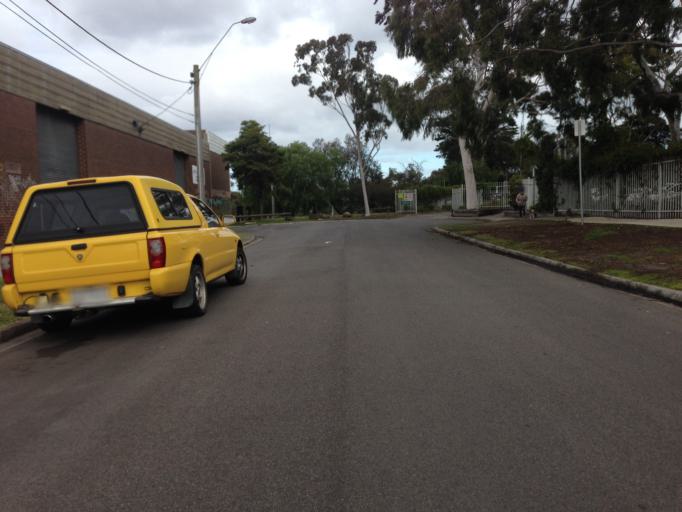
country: AU
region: Victoria
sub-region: Darebin
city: Fairfield
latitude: -37.7831
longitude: 145.0061
